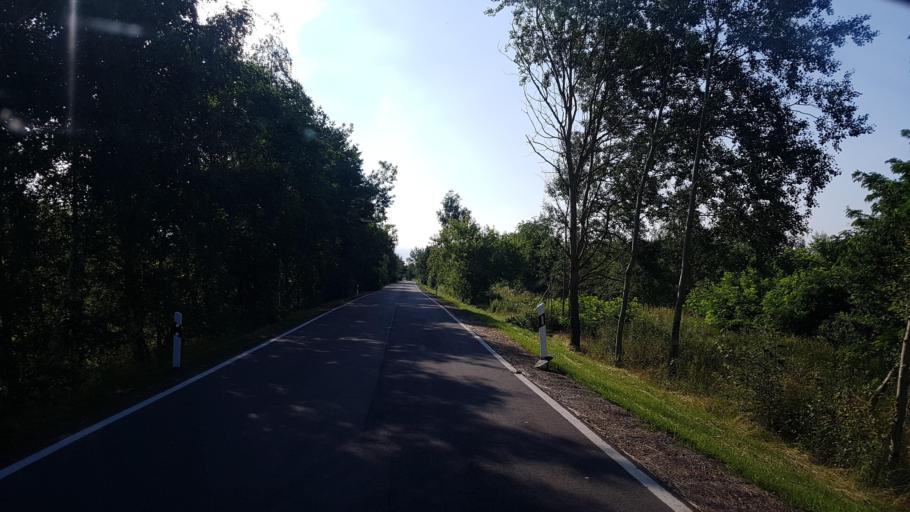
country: DE
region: Brandenburg
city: Grossraschen
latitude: 51.5776
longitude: 14.0192
